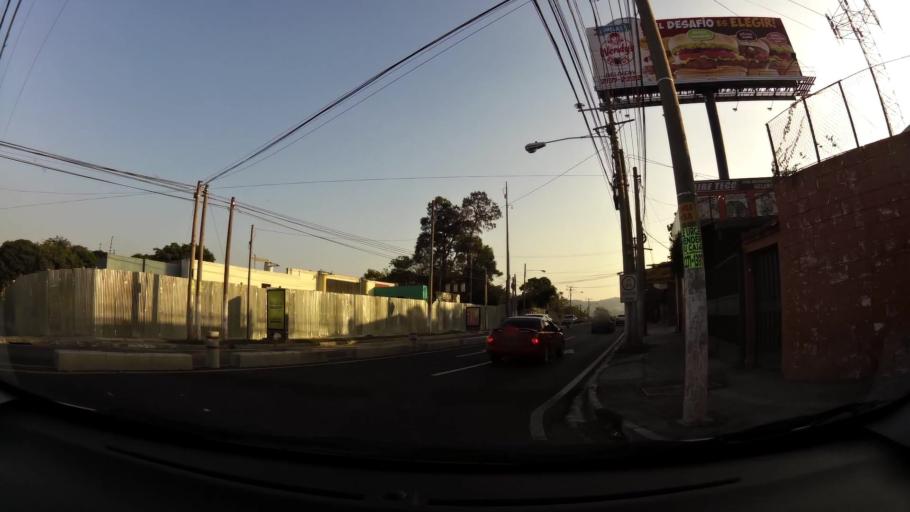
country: SV
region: La Libertad
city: Antiguo Cuscatlan
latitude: 13.6959
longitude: -89.2502
